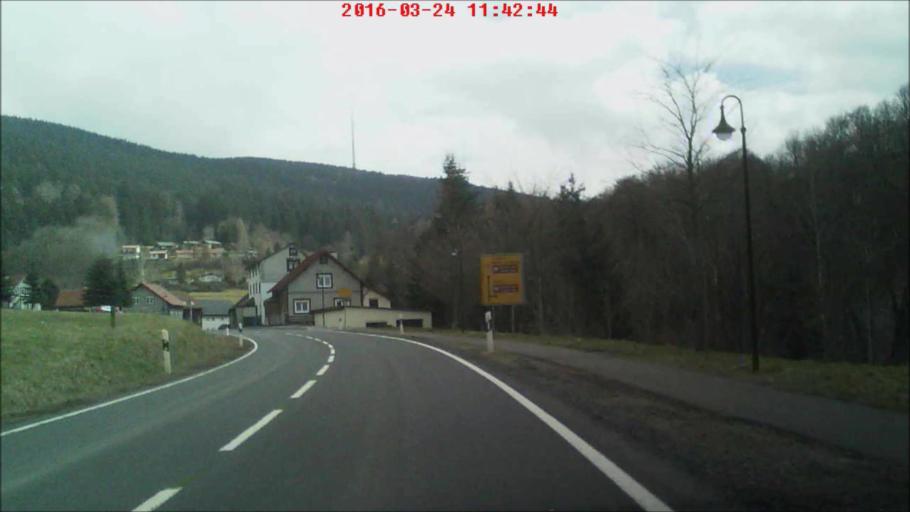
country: DE
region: Thuringia
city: Bachfeld
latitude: 50.4507
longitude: 10.9642
